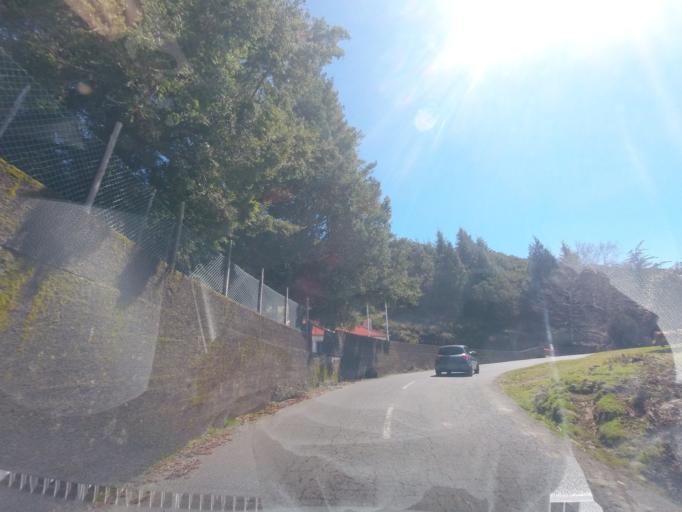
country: PT
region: Madeira
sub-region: Calheta
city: Arco da Calheta
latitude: 32.7400
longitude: -17.1007
